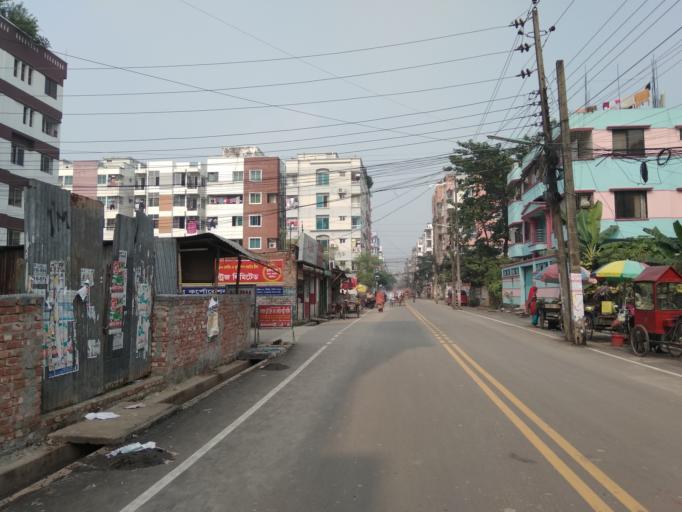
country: BD
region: Dhaka
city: Tungi
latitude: 23.8685
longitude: 90.3833
